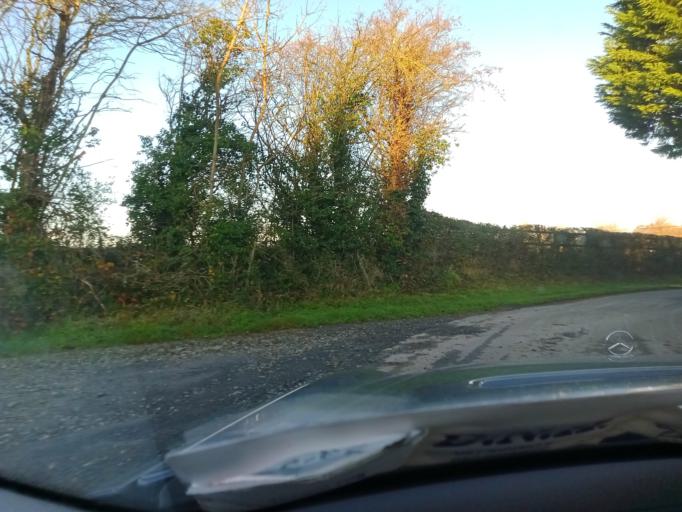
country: IE
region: Leinster
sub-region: Kilkenny
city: Callan
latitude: 52.5452
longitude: -7.3990
